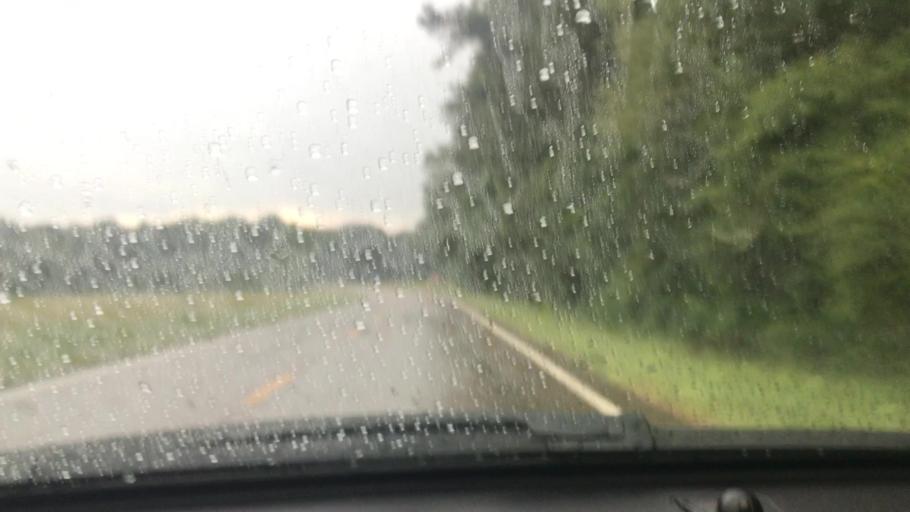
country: US
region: Mississippi
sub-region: Pike County
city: Summit
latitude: 31.3237
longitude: -90.5438
